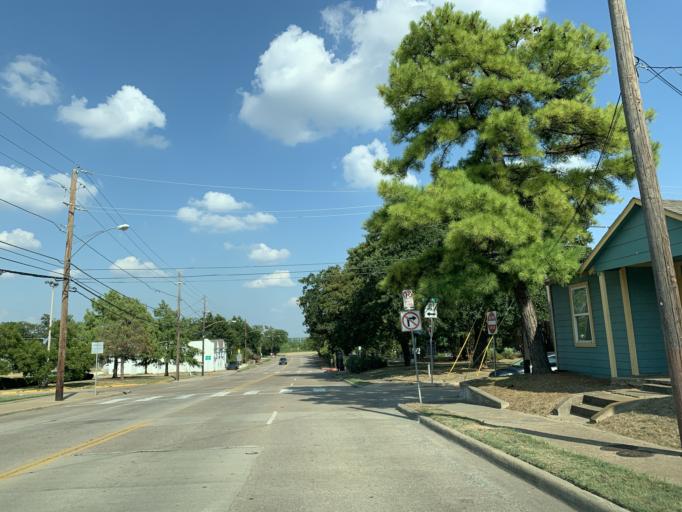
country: US
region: Texas
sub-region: Dallas County
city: Dallas
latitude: 32.7512
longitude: -96.8064
